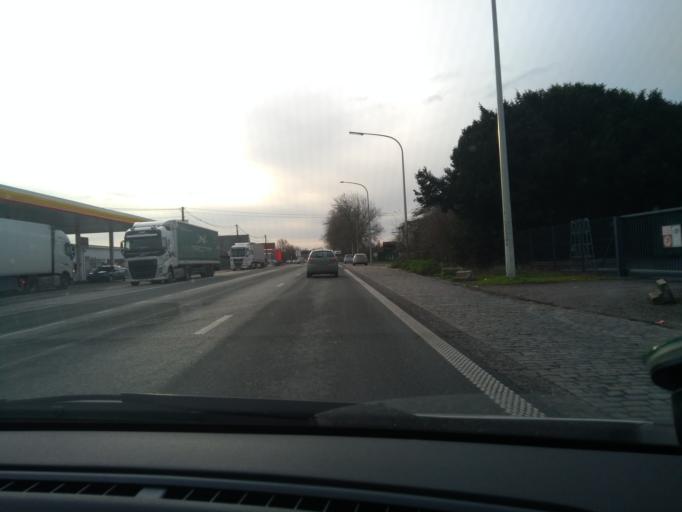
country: BE
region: Wallonia
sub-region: Province du Hainaut
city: Quevy-le-Petit
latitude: 50.3458
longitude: 3.9697
